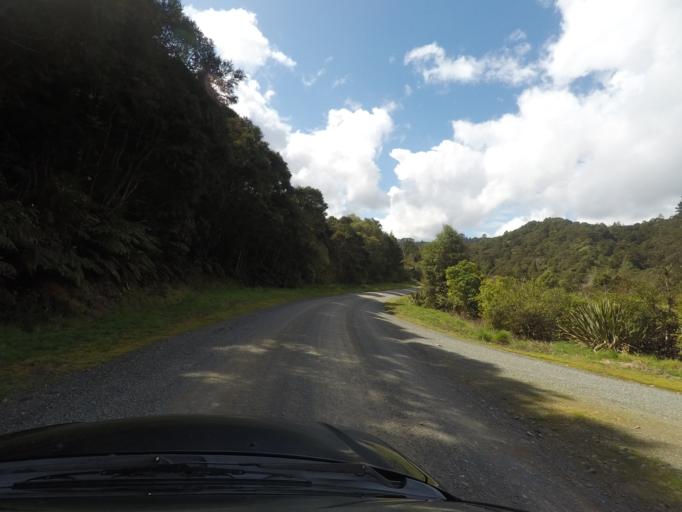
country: NZ
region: Auckland
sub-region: Auckland
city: Red Hill
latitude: -37.0943
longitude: 175.1516
